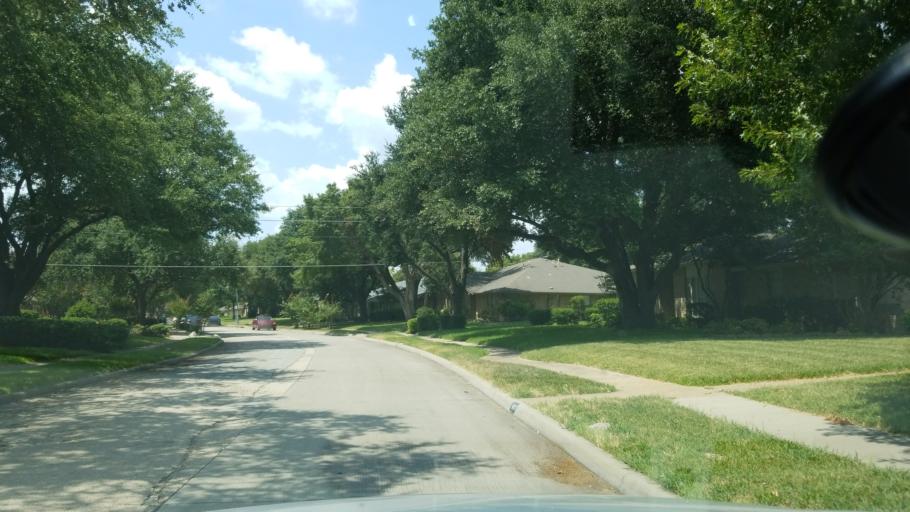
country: US
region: Texas
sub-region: Dallas County
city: Richardson
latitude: 32.9296
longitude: -96.7289
